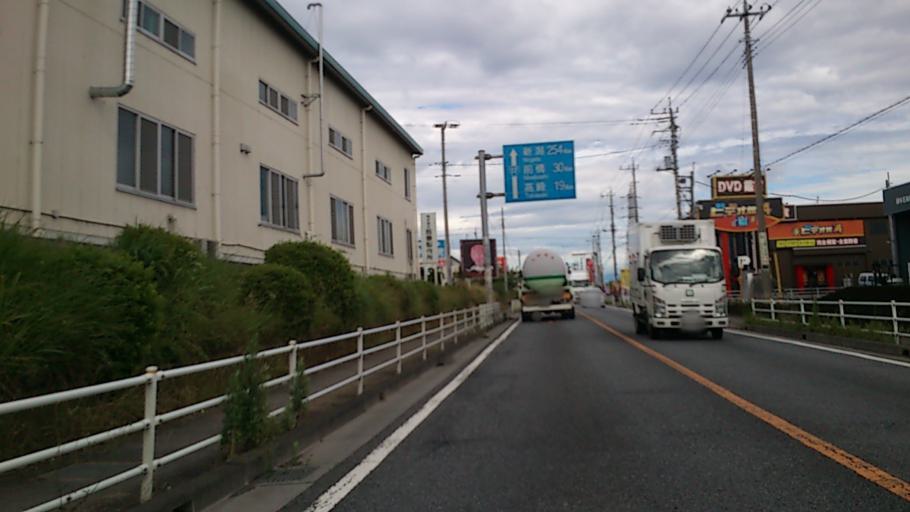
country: JP
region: Saitama
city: Honjo
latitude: 36.2517
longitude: 139.1721
